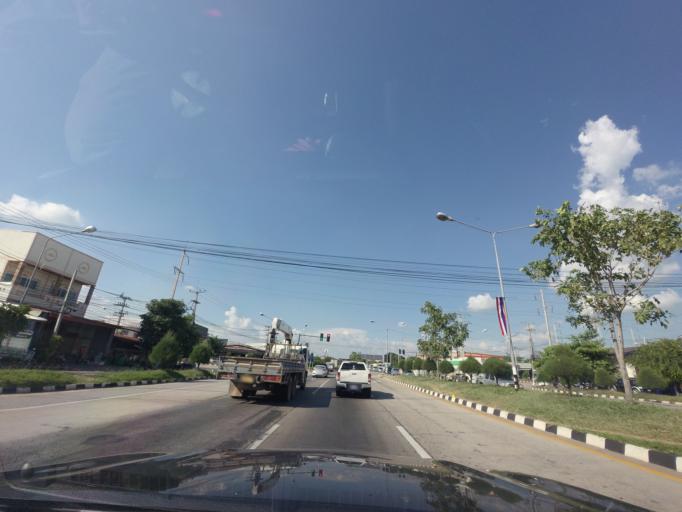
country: TH
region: Nakhon Ratchasima
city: Sida
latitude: 15.5466
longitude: 102.5477
